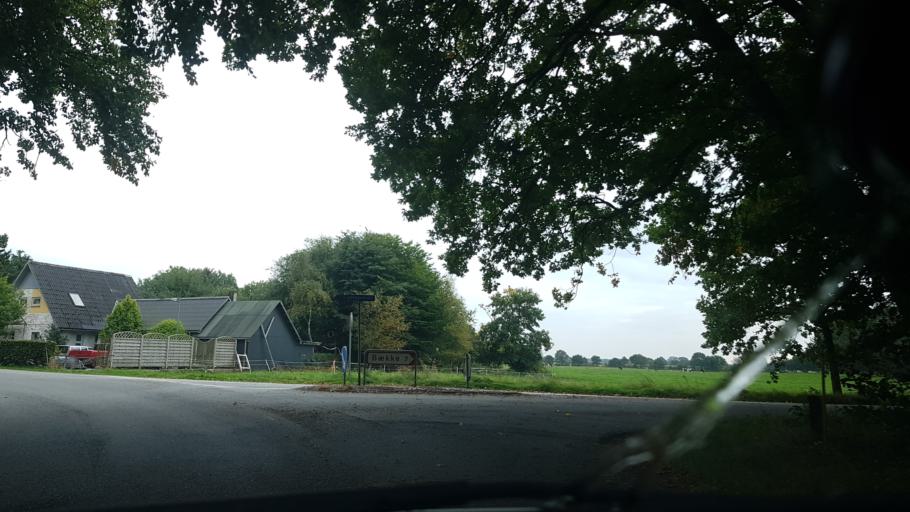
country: DK
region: South Denmark
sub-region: Vejle Kommune
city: Egtved
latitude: 55.5718
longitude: 9.2339
